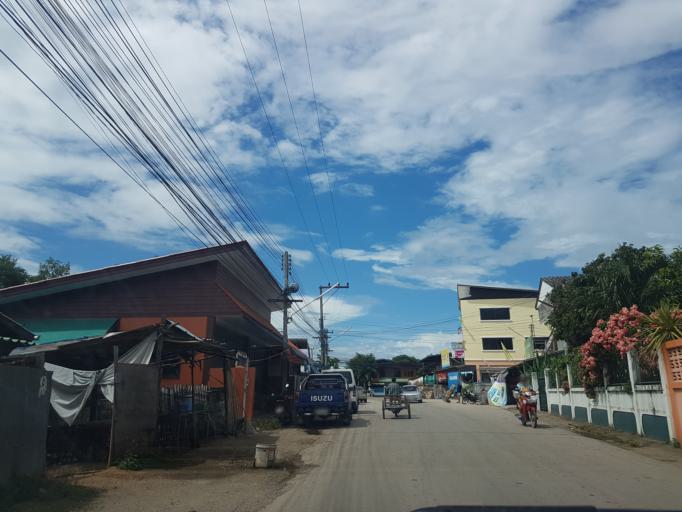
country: TH
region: Lampang
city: Ko Kha
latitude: 18.2417
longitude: 99.4342
